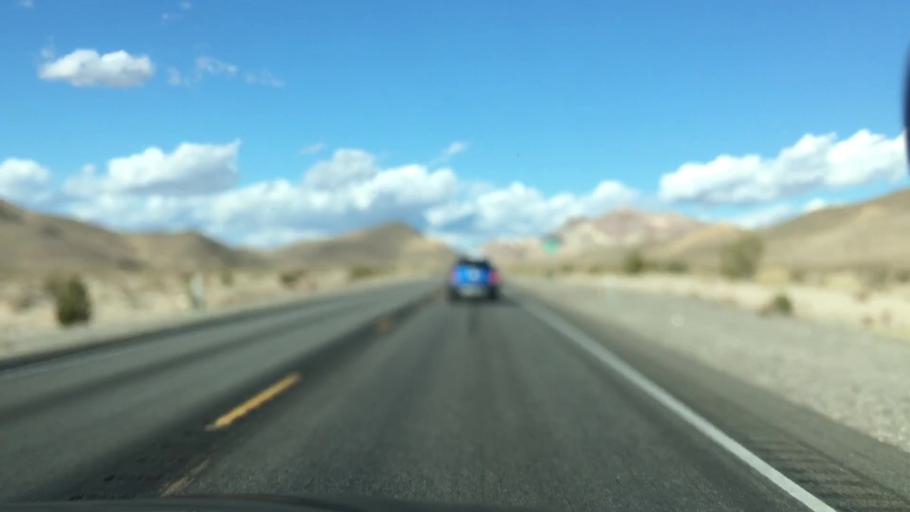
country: US
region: Nevada
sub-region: Nye County
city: Beatty
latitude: 36.8658
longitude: -116.7561
